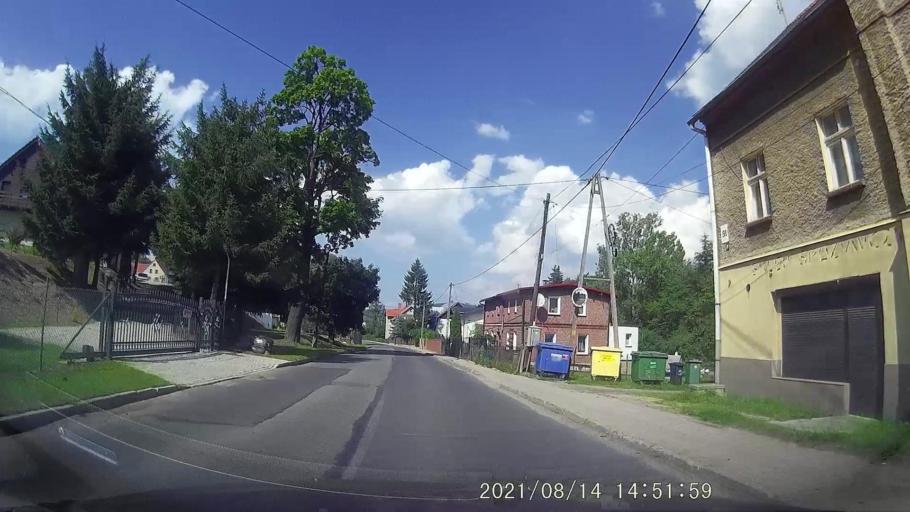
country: PL
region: Lower Silesian Voivodeship
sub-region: Powiat walbrzyski
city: Gluszyca Gorna
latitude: 50.6639
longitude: 16.3757
